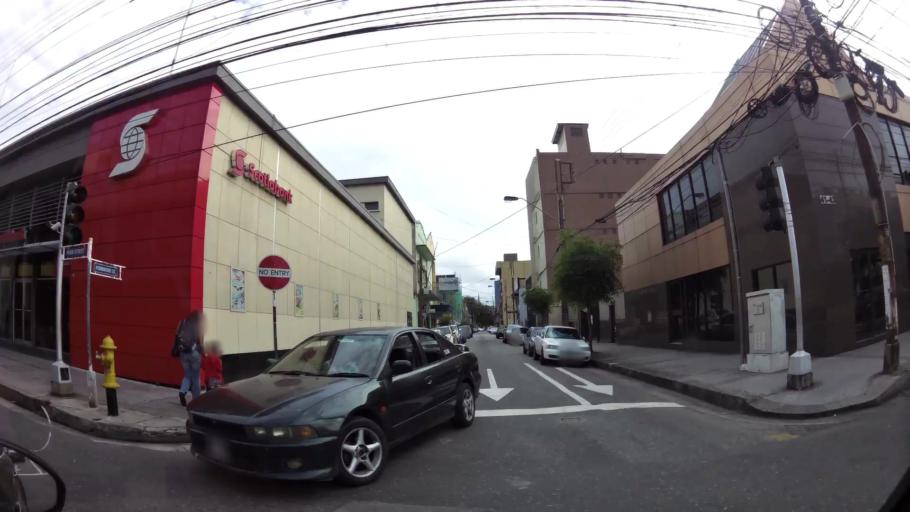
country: TT
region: City of Port of Spain
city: Port-of-Spain
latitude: 10.6566
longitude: -61.5106
